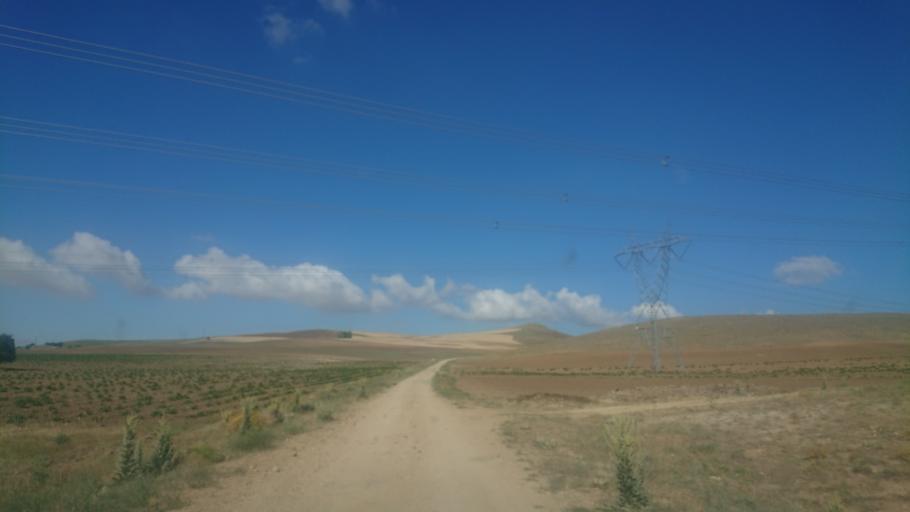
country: TR
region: Aksaray
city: Agacoren
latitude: 38.9144
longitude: 33.9054
